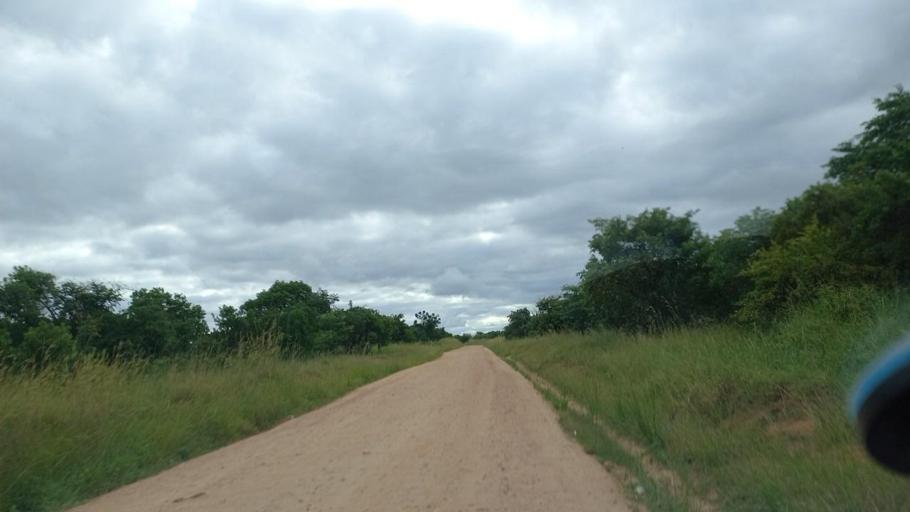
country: ZM
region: Lusaka
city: Chongwe
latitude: -15.4493
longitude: 28.8379
